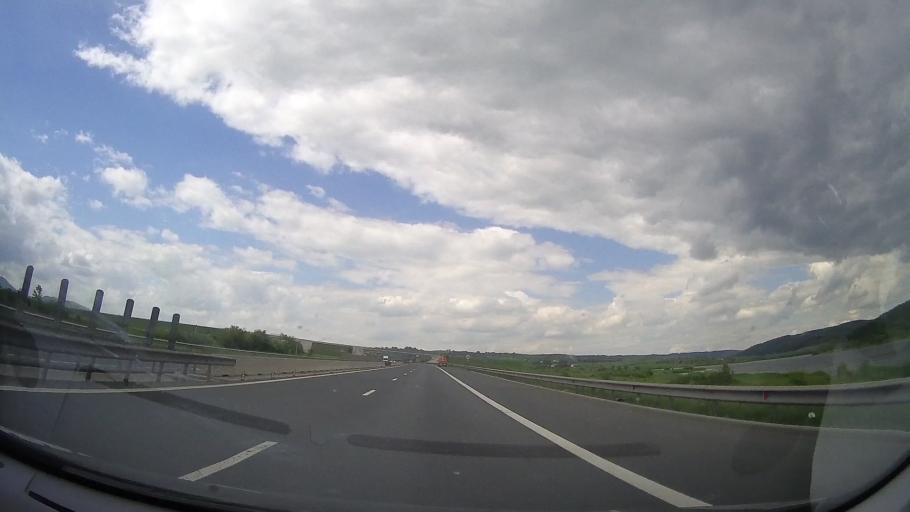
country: RO
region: Sibiu
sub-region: Comuna Orlat
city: Orlat
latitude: 45.7848
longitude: 23.9479
